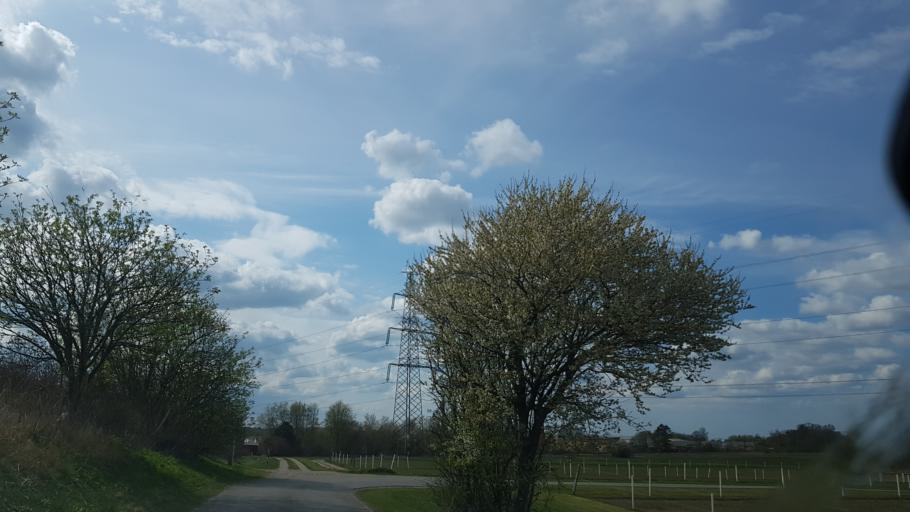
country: DK
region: Capital Region
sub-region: Allerod Kommune
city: Lillerod
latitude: 55.8912
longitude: 12.3416
